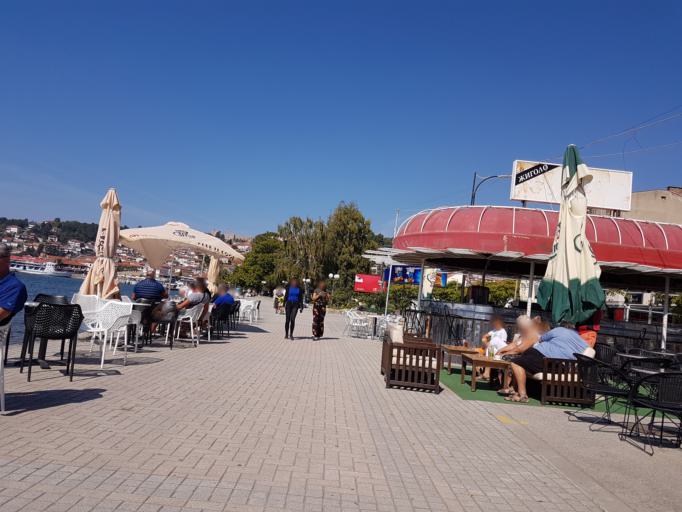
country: MK
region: Ohrid
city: Ohrid
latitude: 41.1112
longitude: 20.8024
